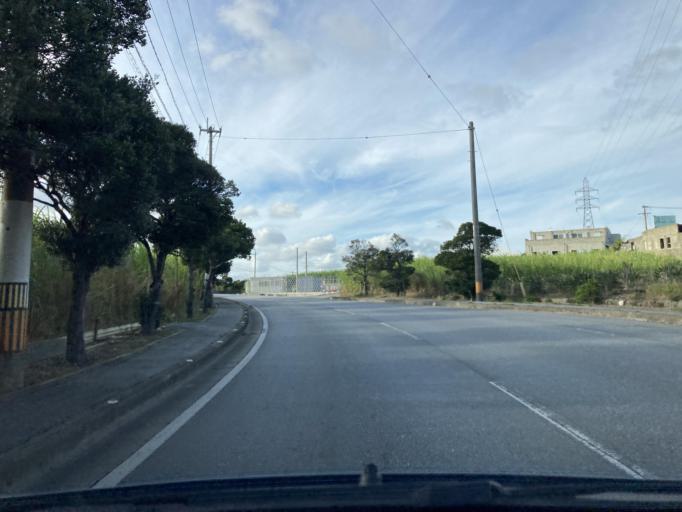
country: JP
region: Okinawa
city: Tomigusuku
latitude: 26.1569
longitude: 127.7397
